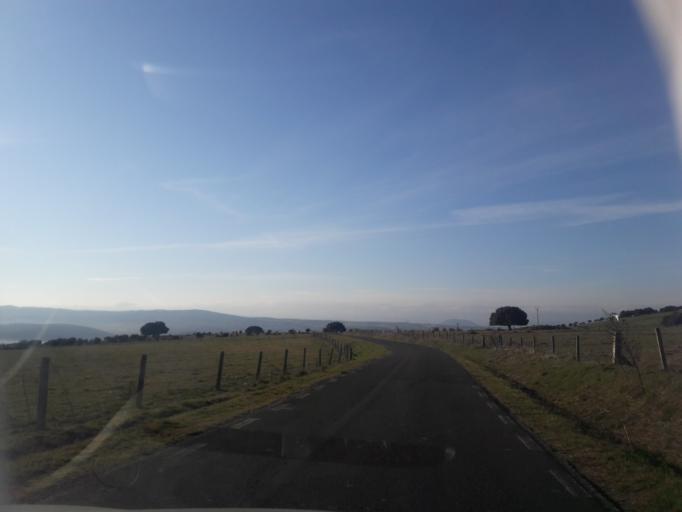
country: ES
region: Castille and Leon
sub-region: Provincia de Salamanca
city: Salvatierra de Tormes
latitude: 40.6107
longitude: -5.6029
